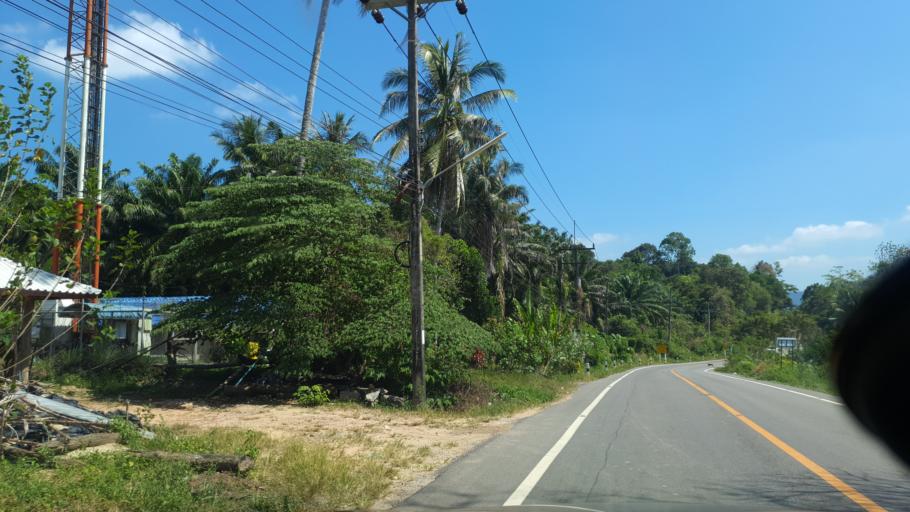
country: TH
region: Krabi
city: Khlong Thom
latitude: 7.9216
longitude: 99.2485
